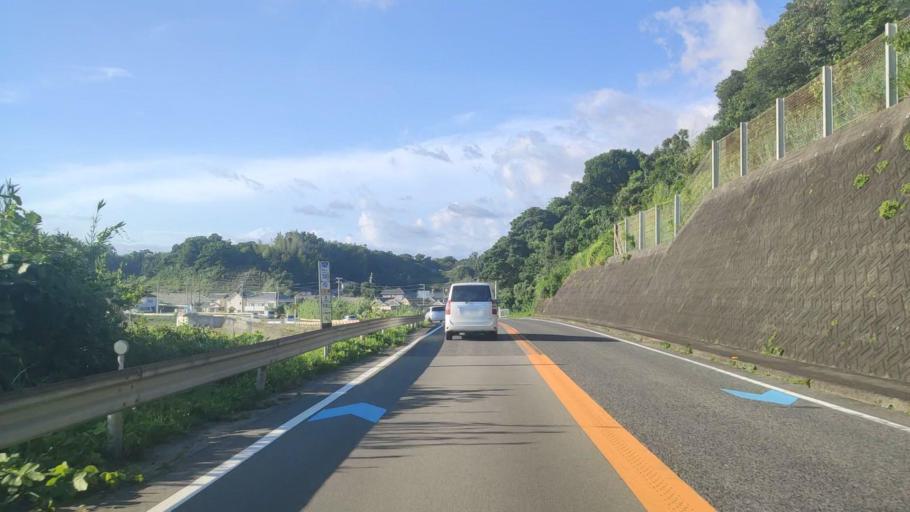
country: JP
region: Wakayama
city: Tanabe
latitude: 33.7463
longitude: 135.3292
